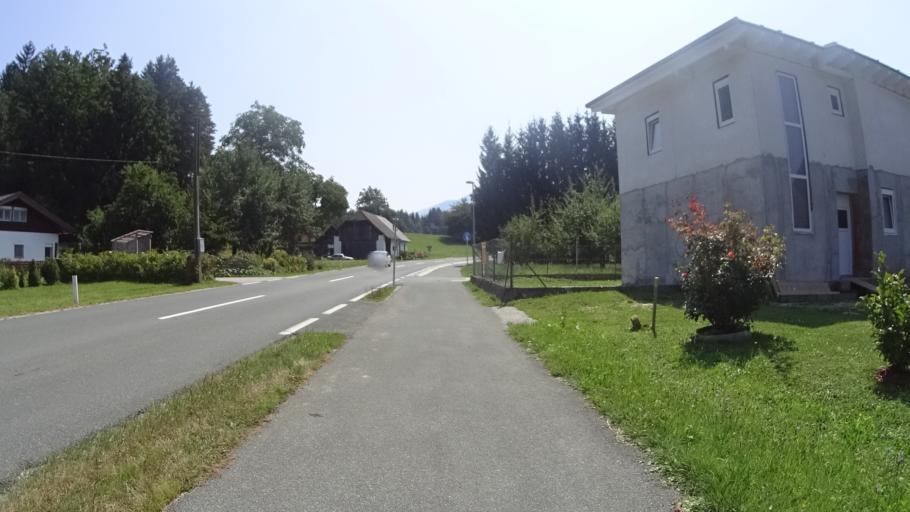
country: AT
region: Carinthia
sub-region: Politischer Bezirk Volkermarkt
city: Eberndorf
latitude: 46.5734
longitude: 14.6596
